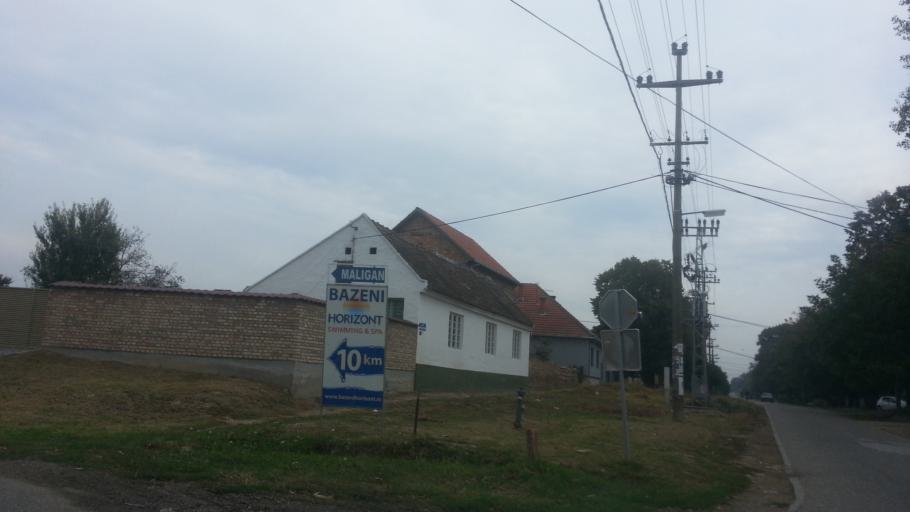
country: RS
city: Belegis
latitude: 45.0214
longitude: 20.3364
